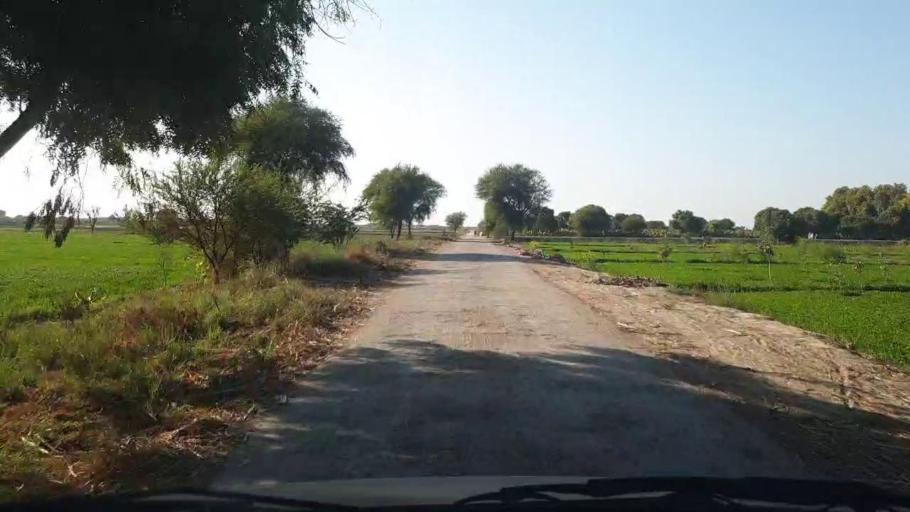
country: PK
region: Sindh
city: Samaro
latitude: 25.3576
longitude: 69.3019
